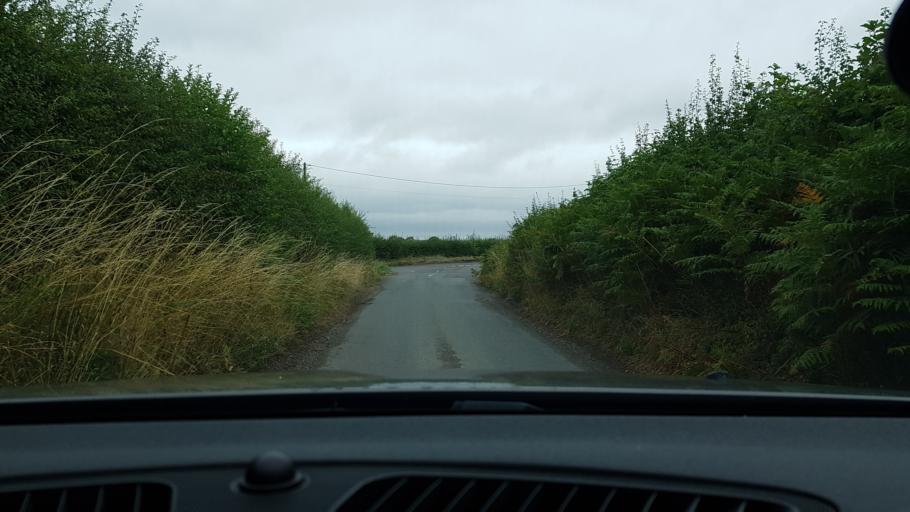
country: GB
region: England
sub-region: Wiltshire
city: Shalbourne
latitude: 51.3788
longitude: -1.5361
